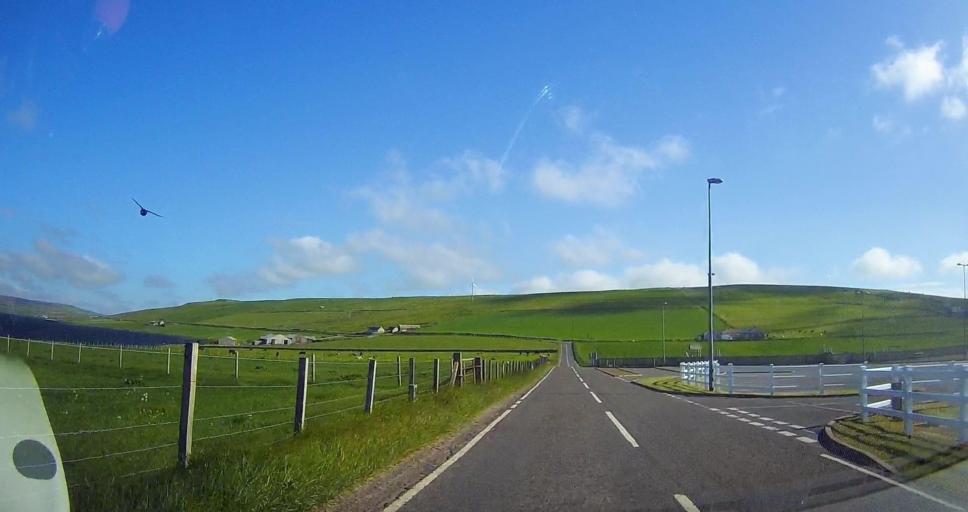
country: GB
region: Scotland
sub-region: Orkney Islands
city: Stromness
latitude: 59.1200
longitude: -3.3059
